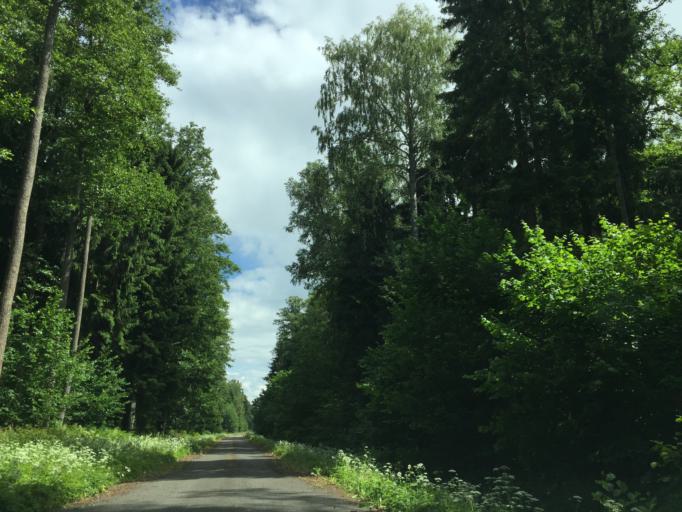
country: LV
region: Saulkrastu
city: Saulkrasti
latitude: 57.3490
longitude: 24.4163
